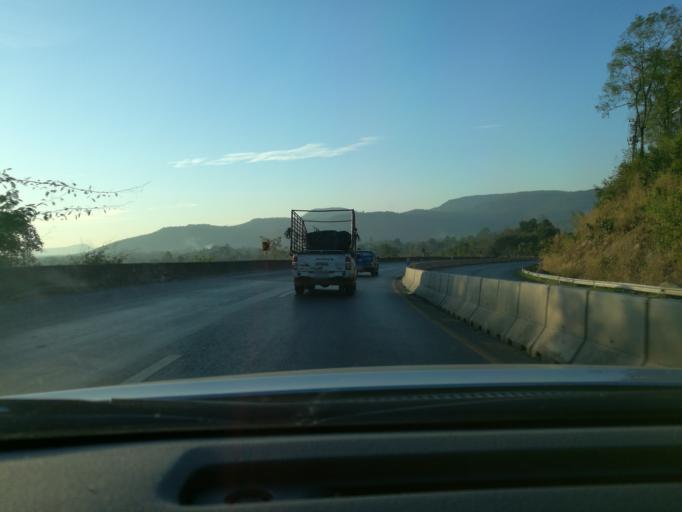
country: TH
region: Phitsanulok
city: Wang Thong
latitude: 16.8555
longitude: 100.5077
